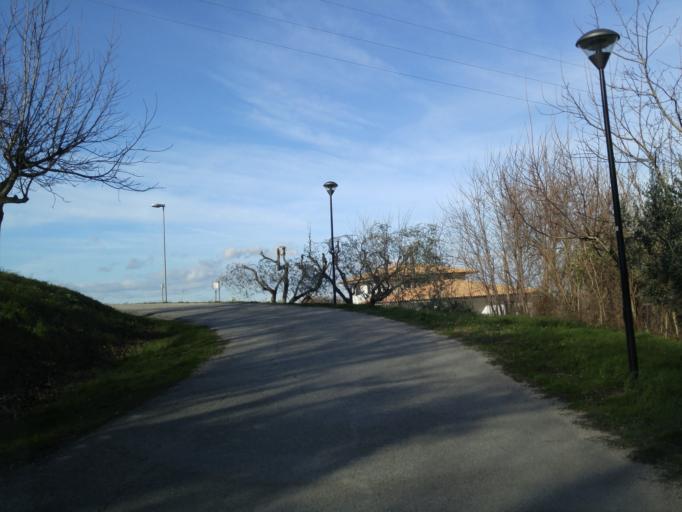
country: IT
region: The Marches
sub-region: Provincia di Pesaro e Urbino
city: Cartoceto
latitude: 43.7693
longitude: 12.8814
